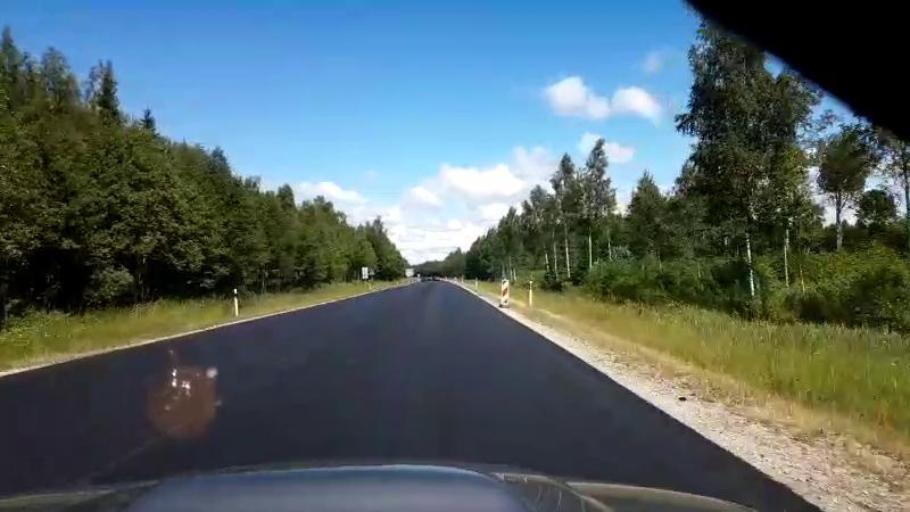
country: LV
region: Salacgrivas
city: Ainazi
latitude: 58.0138
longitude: 24.4937
